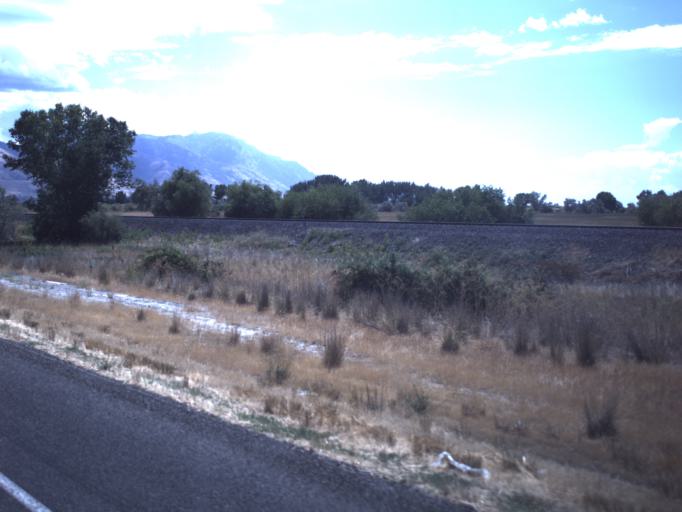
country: US
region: Utah
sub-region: Box Elder County
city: Honeyville
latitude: 41.5481
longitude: -112.1009
